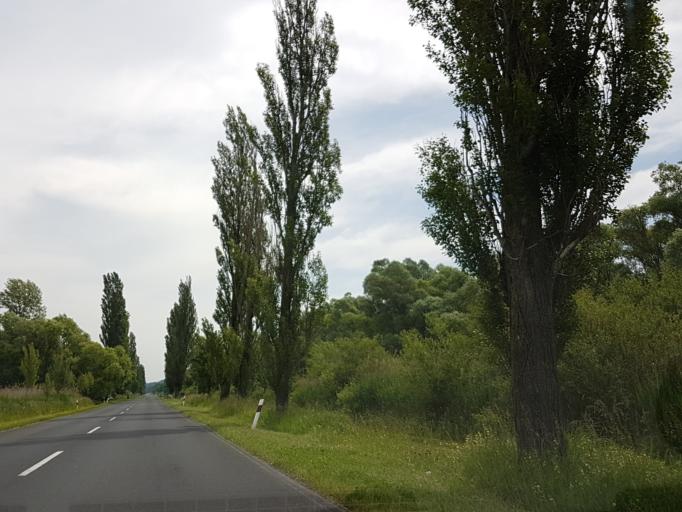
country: HU
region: Veszprem
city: Tapolca
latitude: 46.8020
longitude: 17.3947
